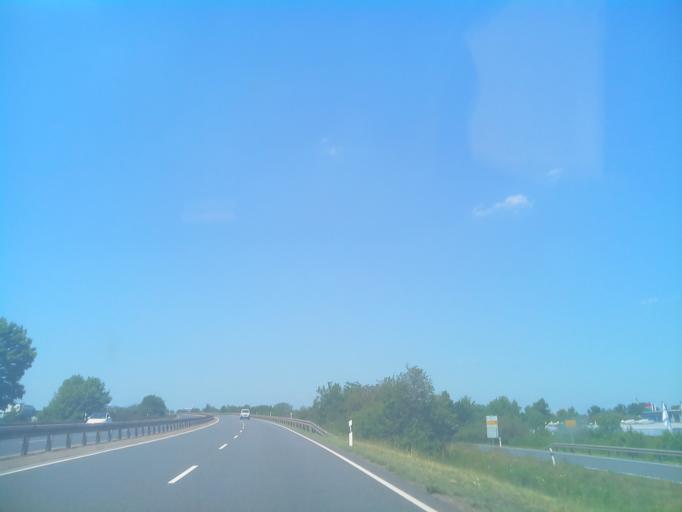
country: DE
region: Bavaria
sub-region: Regierungsbezirk Unterfranken
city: Schweinfurt
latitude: 50.0304
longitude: 10.2340
